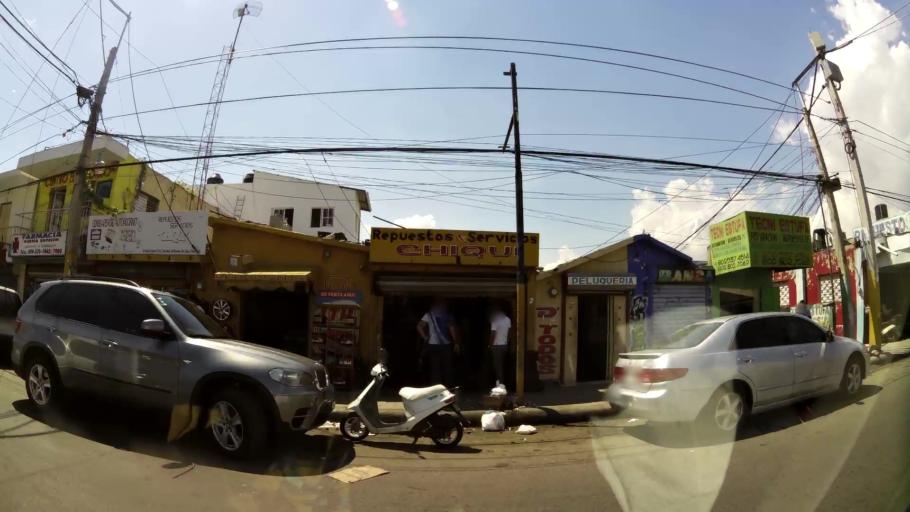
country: DO
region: Nacional
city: Bella Vista
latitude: 18.4604
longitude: -69.9765
